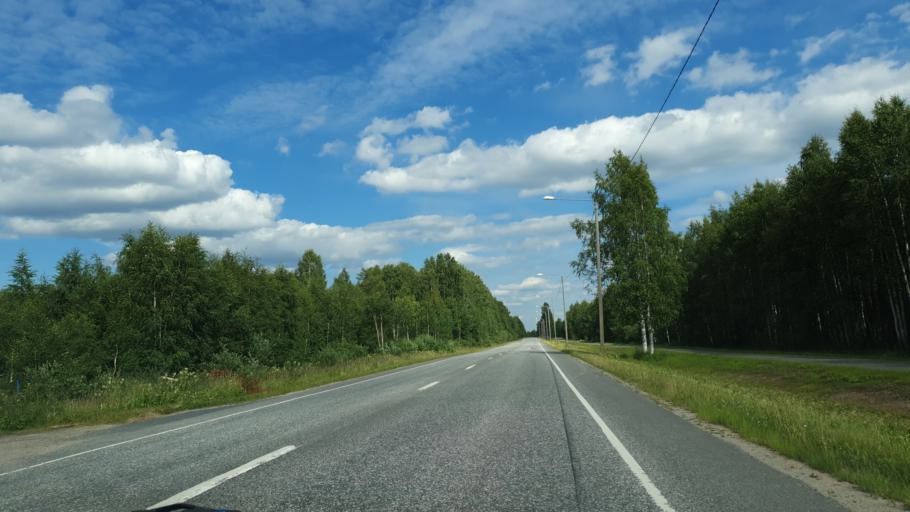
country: FI
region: Kainuu
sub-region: Kajaani
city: Kajaani
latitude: 64.2530
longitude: 27.7954
